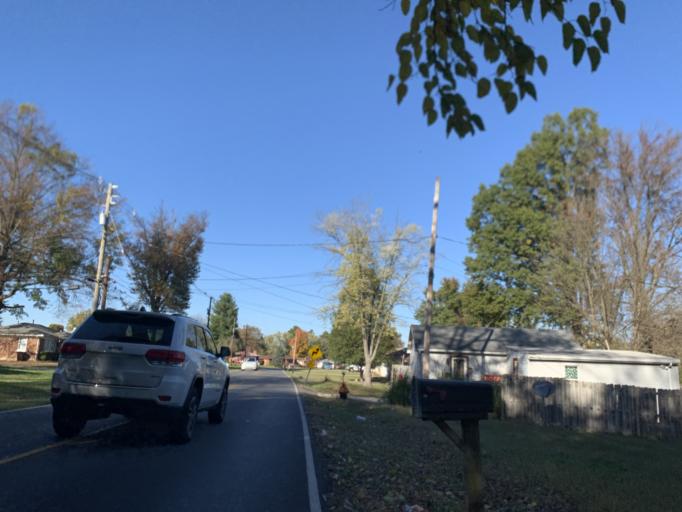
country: US
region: Kentucky
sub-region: Jefferson County
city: Pleasure Ridge Park
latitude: 38.1626
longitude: -85.8446
